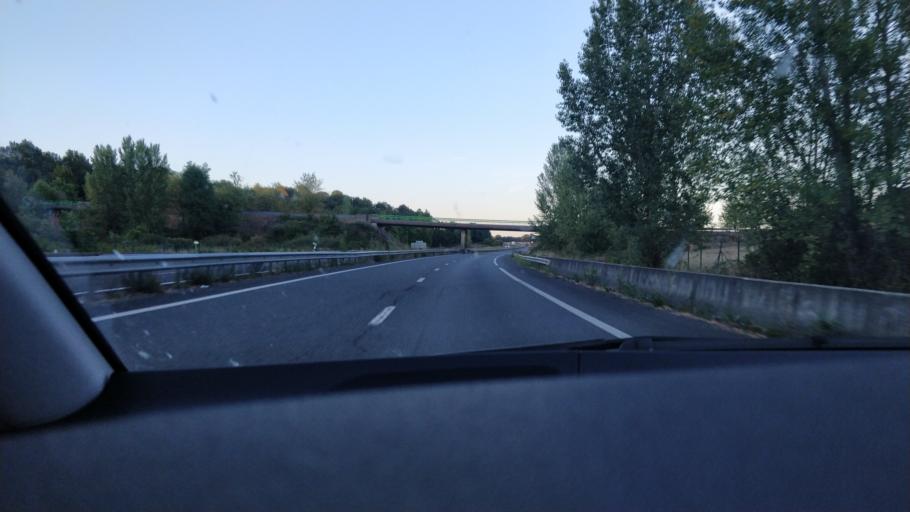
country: FR
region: Poitou-Charentes
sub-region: Departement de la Charente
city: Taponnat-Fleurignac
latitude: 45.7831
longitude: 0.4091
